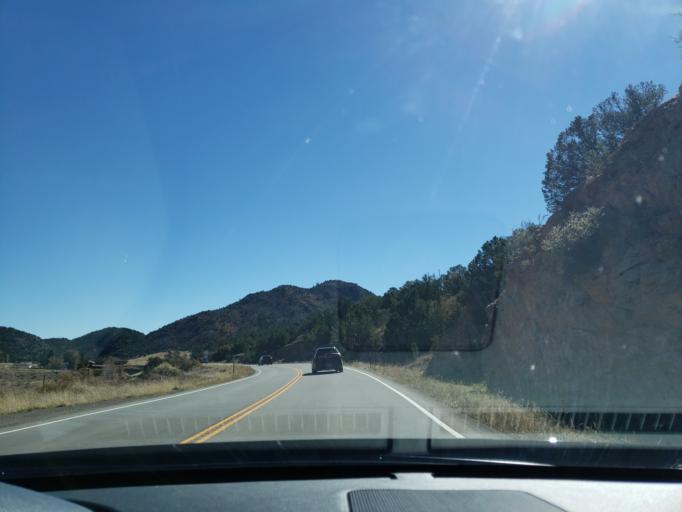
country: US
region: Colorado
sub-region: Fremont County
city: Canon City
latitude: 38.5881
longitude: -105.4220
